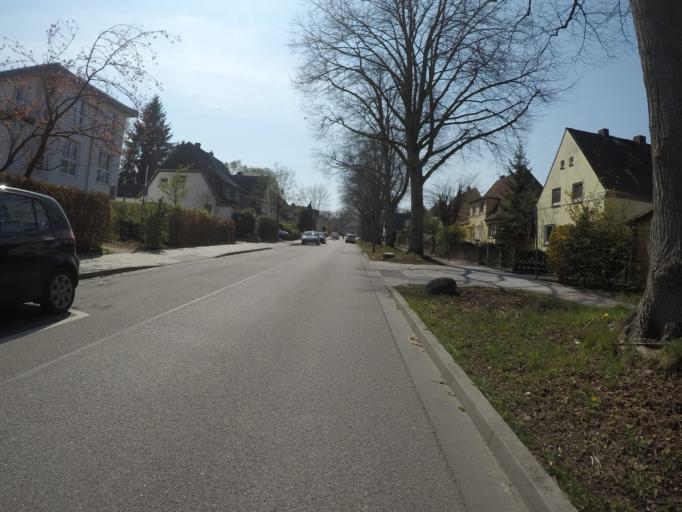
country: DE
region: Schleswig-Holstein
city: Halstenbek
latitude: 53.5791
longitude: 9.8164
